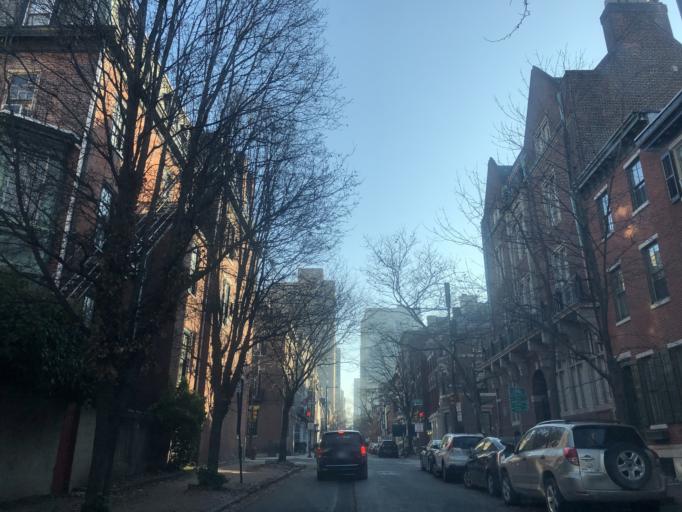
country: US
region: Pennsylvania
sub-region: Philadelphia County
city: Philadelphia
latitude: 39.9500
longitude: -75.1782
